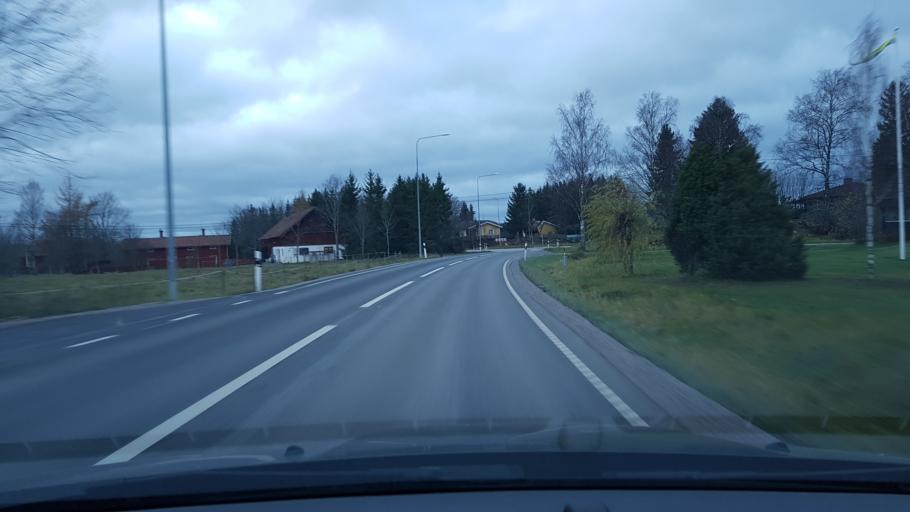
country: SE
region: Uppsala
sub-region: Uppsala Kommun
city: Vattholma
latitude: 59.9516
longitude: 17.8985
